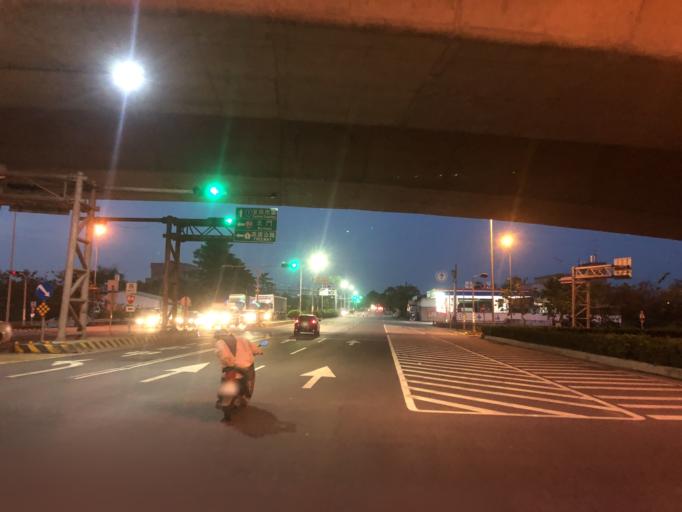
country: TW
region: Taiwan
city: Yujing
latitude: 23.1633
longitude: 120.3411
